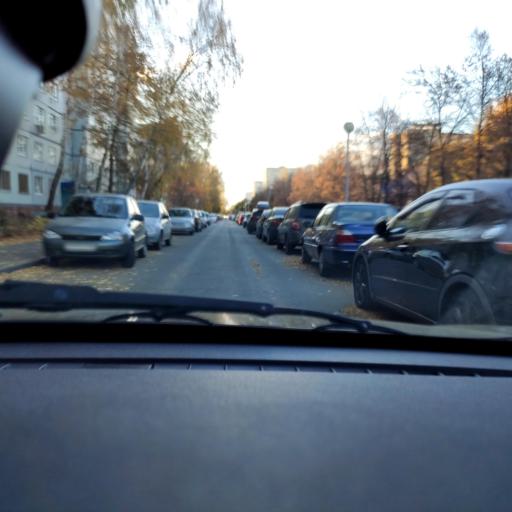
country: RU
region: Samara
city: Tol'yatti
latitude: 53.5241
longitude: 49.3162
